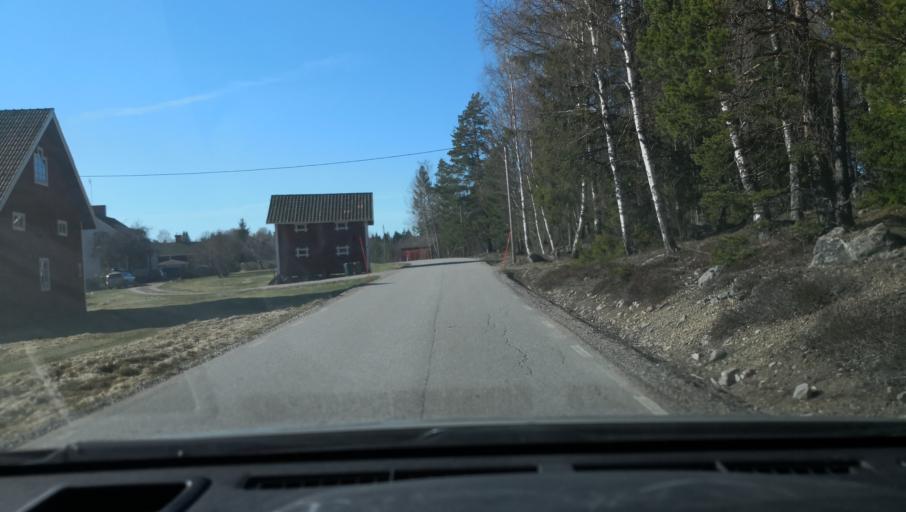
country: SE
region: Vaestmanland
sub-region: Sala Kommun
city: Sala
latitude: 60.0811
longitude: 16.4569
